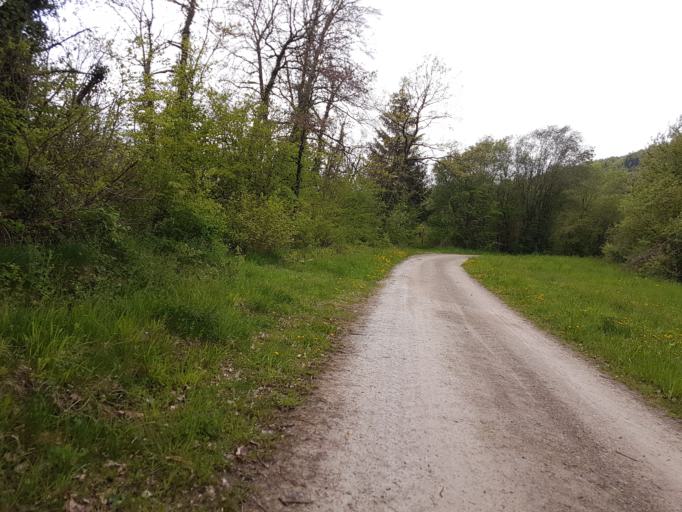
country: CH
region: Schaffhausen
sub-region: Bezirk Schleitheim
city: Schleitheim
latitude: 47.7653
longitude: 8.4749
